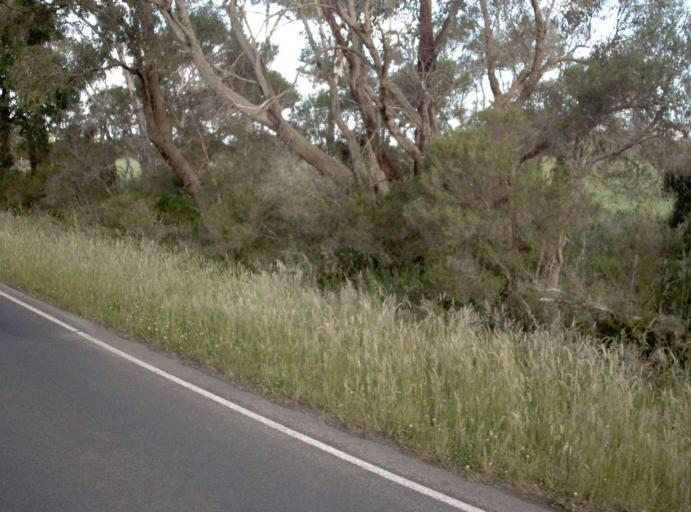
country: AU
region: Victoria
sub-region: Bass Coast
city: North Wonthaggi
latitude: -38.5963
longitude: 145.7864
